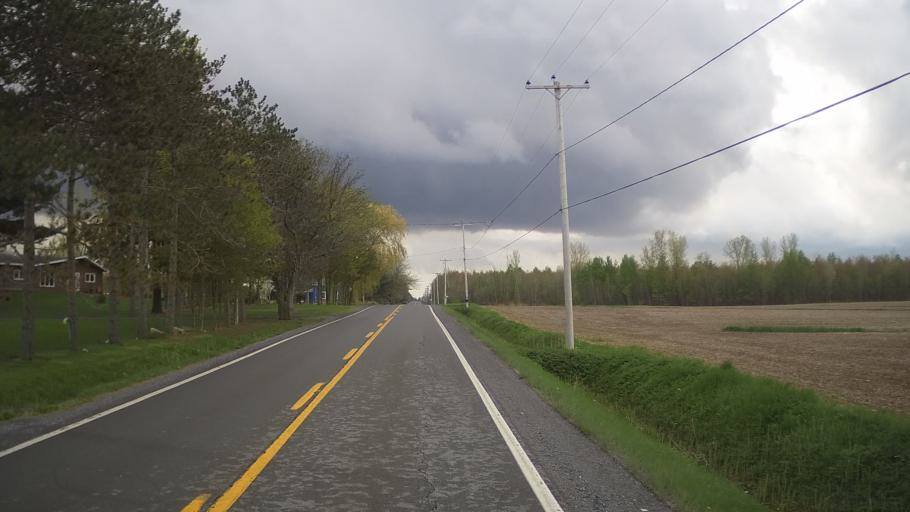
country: CA
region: Quebec
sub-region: Monteregie
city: Marieville
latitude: 45.3257
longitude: -73.1083
